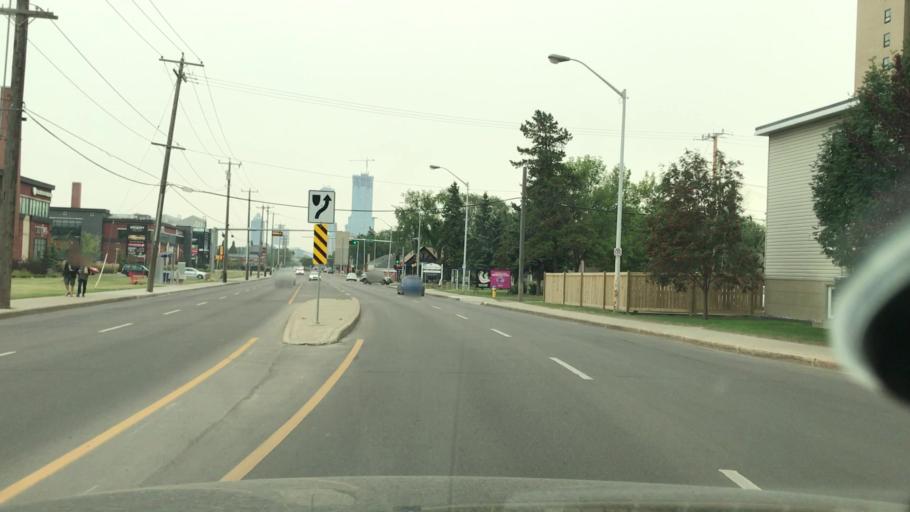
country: CA
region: Alberta
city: Edmonton
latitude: 53.5462
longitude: -113.5304
